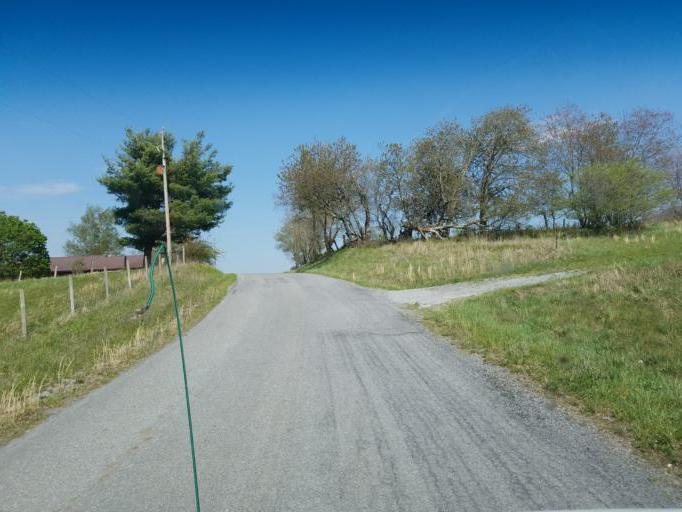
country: US
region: Virginia
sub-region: Smyth County
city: Marion
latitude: 36.7619
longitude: -81.4620
